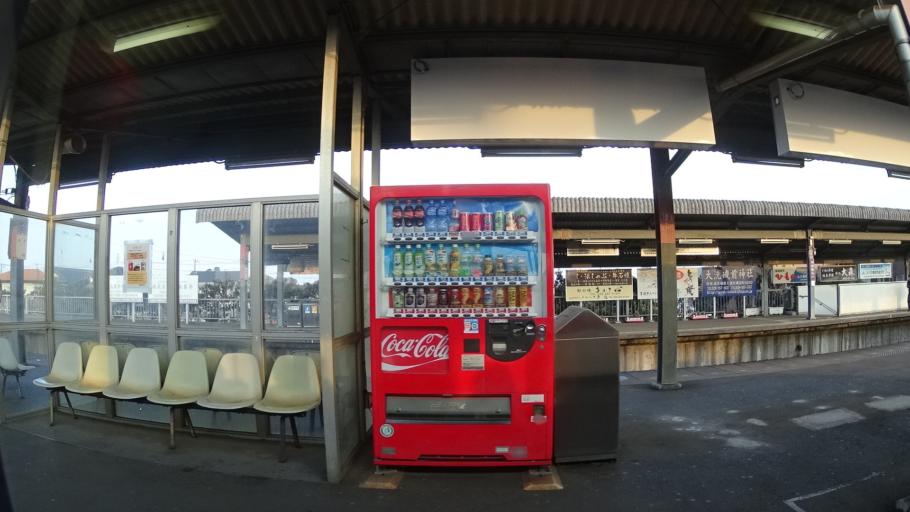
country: JP
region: Ibaraki
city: Oarai
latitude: 36.3154
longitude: 140.5627
